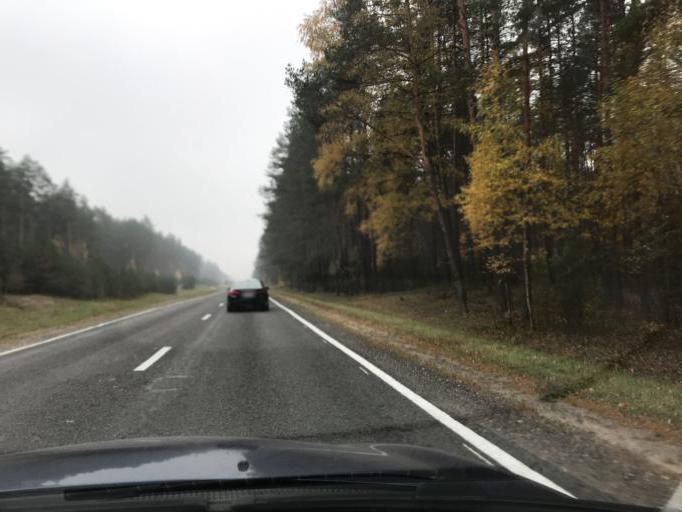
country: LT
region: Alytaus apskritis
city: Druskininkai
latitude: 53.8669
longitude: 23.8940
